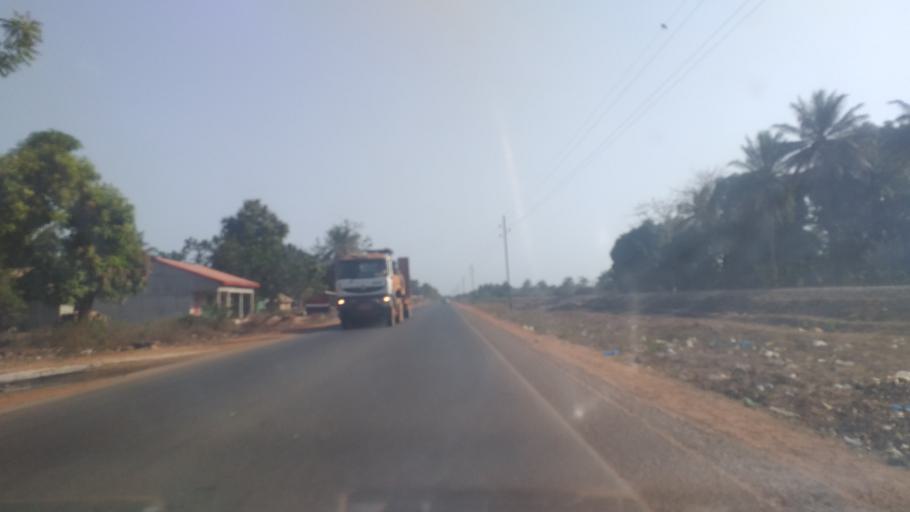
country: GN
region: Boke
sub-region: Boke Prefecture
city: Kamsar
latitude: 10.7181
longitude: -14.5213
